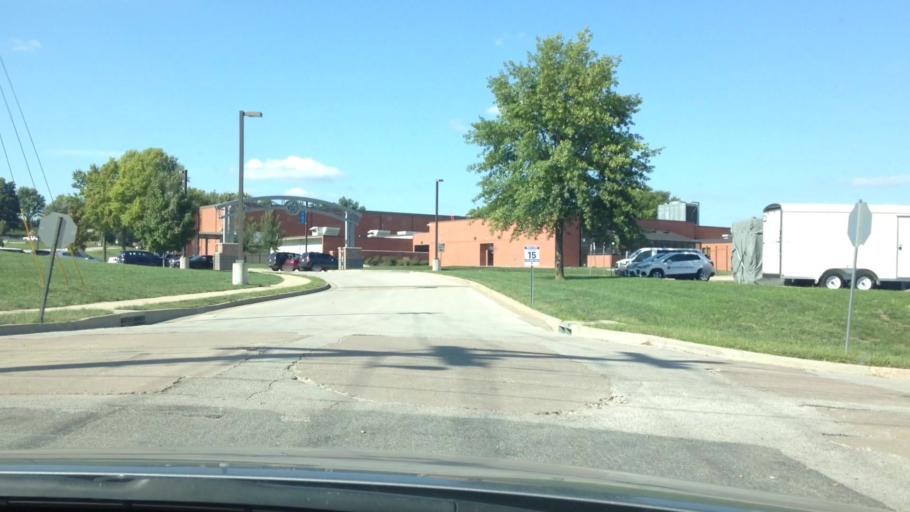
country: US
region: Kansas
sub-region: Leavenworth County
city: Leavenworth
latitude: 39.2948
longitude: -94.9300
